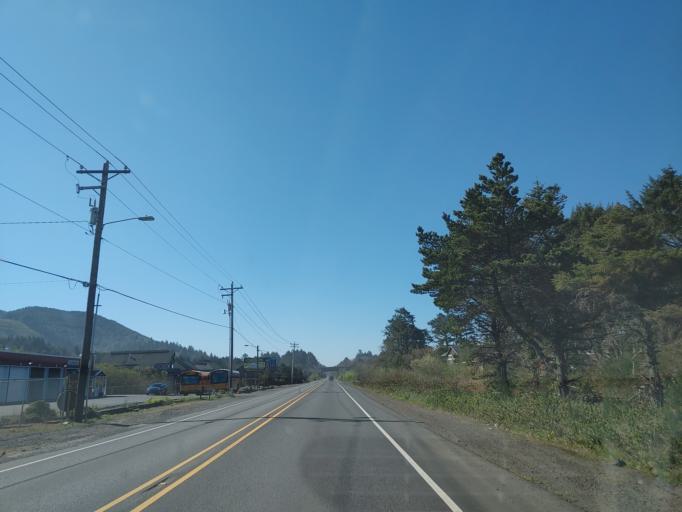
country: US
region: Oregon
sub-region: Tillamook County
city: Rockaway Beach
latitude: 45.5971
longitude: -123.9466
